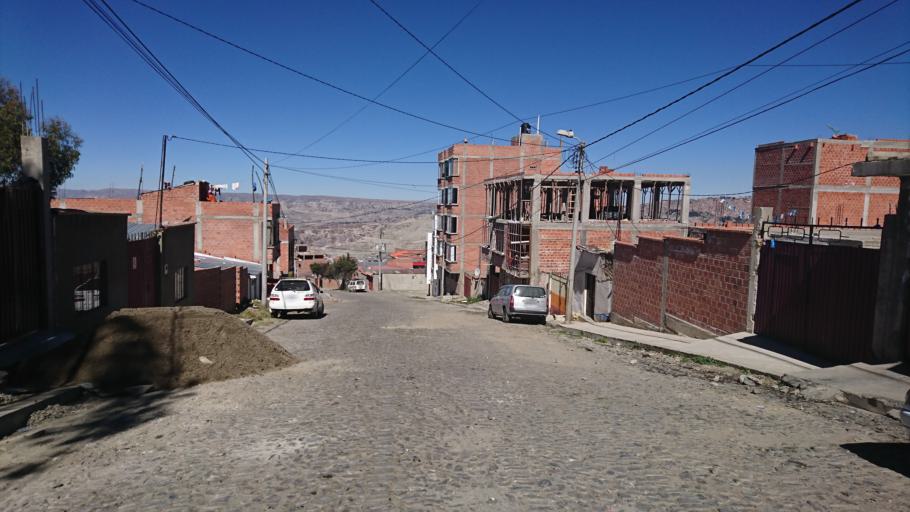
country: BO
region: La Paz
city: La Paz
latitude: -16.4889
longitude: -68.1034
